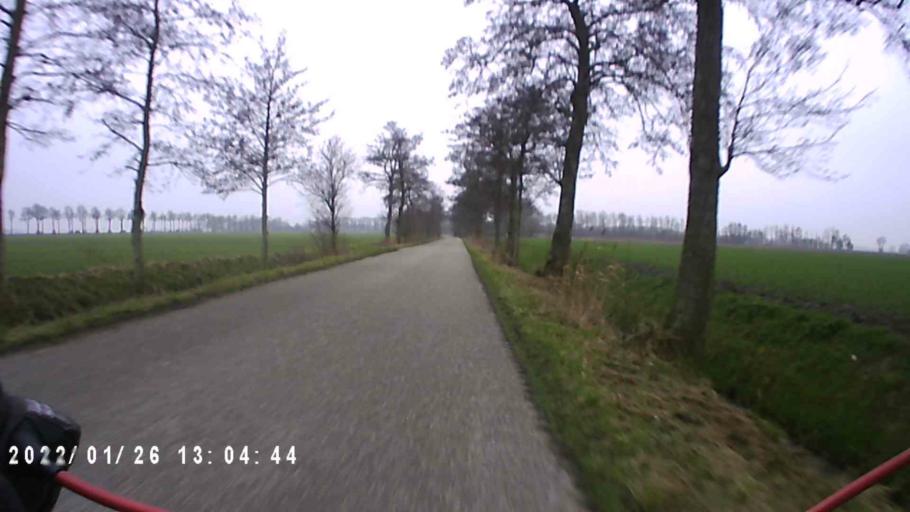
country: NL
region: Groningen
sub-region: Gemeente Zuidhorn
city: Oldehove
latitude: 53.3539
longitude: 6.4412
